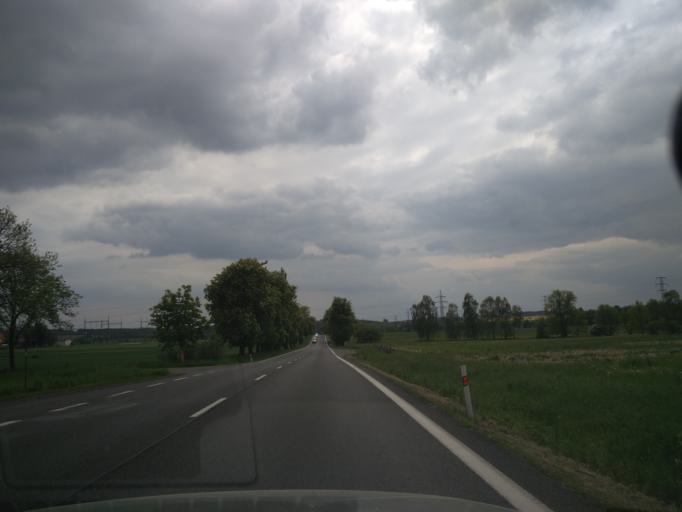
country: CZ
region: Central Bohemia
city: Milin
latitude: 49.5991
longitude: 14.0654
